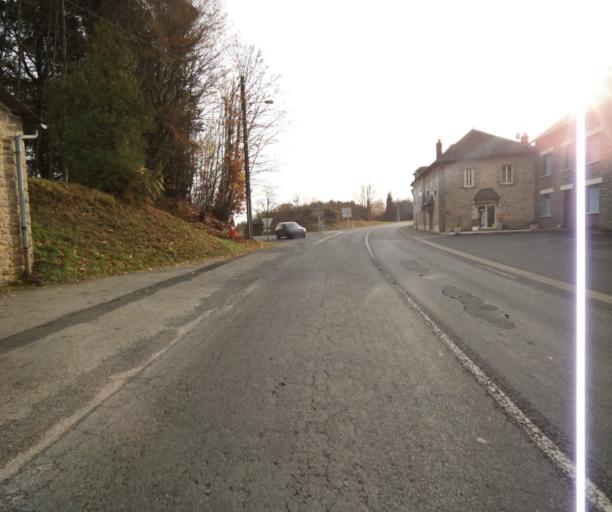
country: FR
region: Limousin
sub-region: Departement de la Correze
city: Sainte-Fortunade
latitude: 45.1963
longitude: 1.7741
